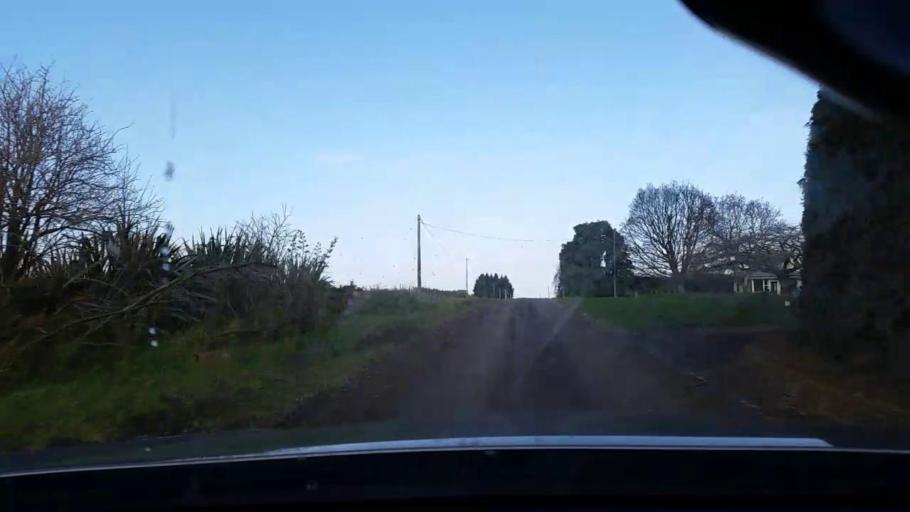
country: NZ
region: Southland
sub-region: Southland District
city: Winton
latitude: -46.2769
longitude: 168.2930
